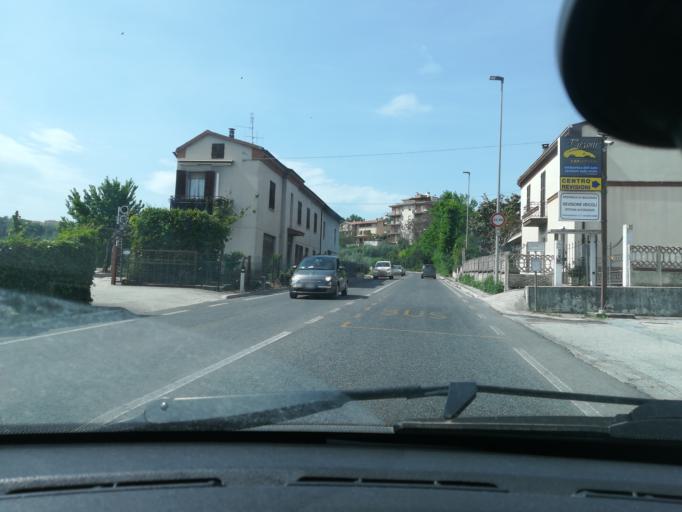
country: IT
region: The Marches
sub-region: Provincia di Macerata
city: Macerata
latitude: 43.2901
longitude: 13.4711
